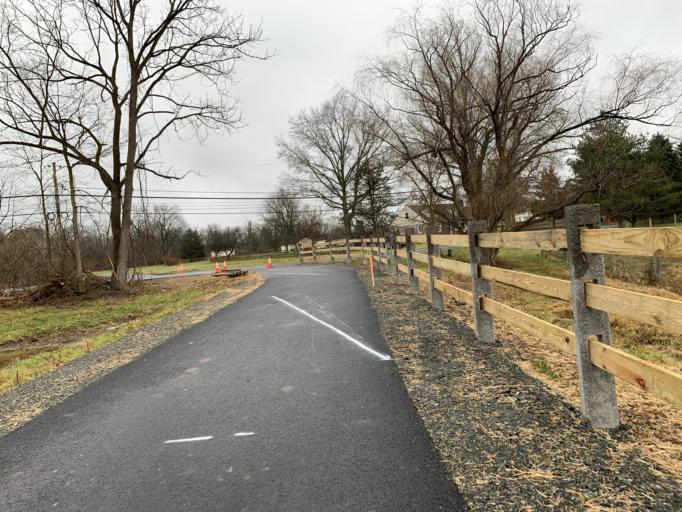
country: US
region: Pennsylvania
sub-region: Montgomery County
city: Sanatoga
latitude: 40.2249
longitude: -75.6008
